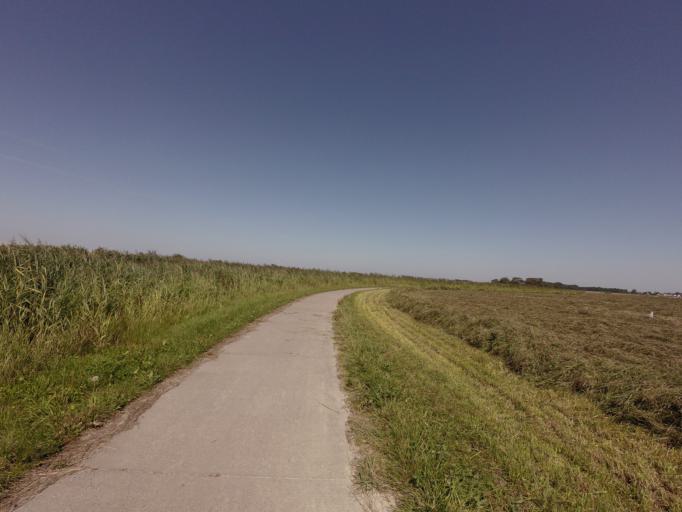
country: NL
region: Friesland
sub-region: Gemeente Dongeradeel
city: Anjum
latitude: 53.3926
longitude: 6.0683
